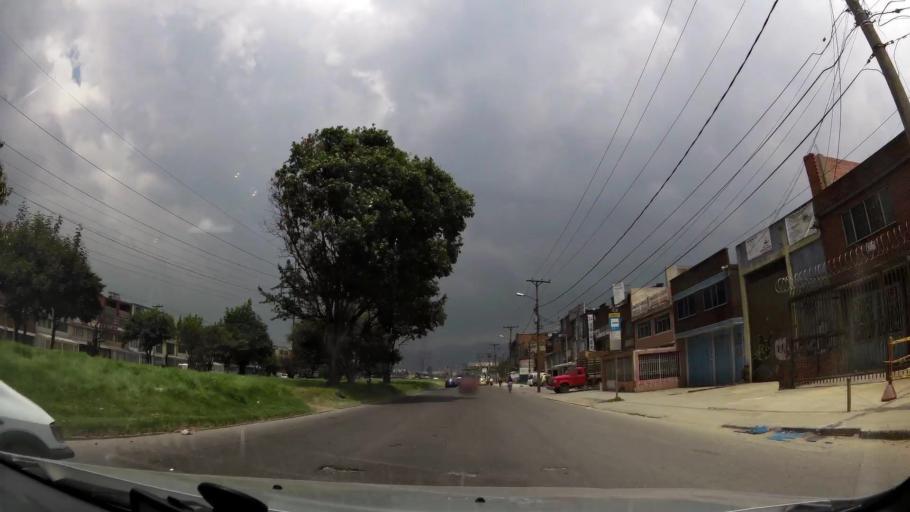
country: CO
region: Bogota D.C.
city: Bogota
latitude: 4.6176
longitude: -74.1074
